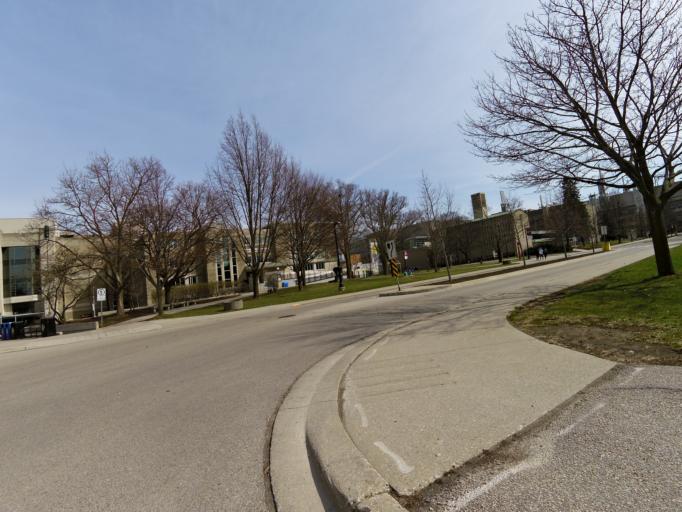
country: CA
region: Ontario
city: Hamilton
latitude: 43.2629
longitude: -79.9190
